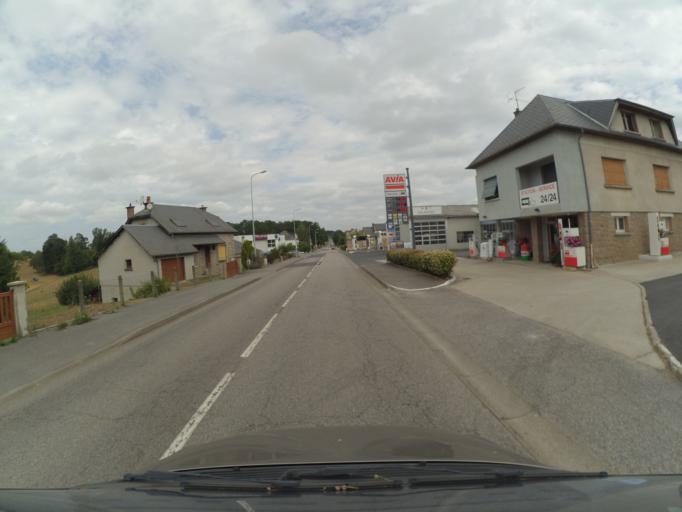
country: FR
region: Limousin
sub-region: Departement de la Correze
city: Ussel
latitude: 45.5570
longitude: 2.3020
